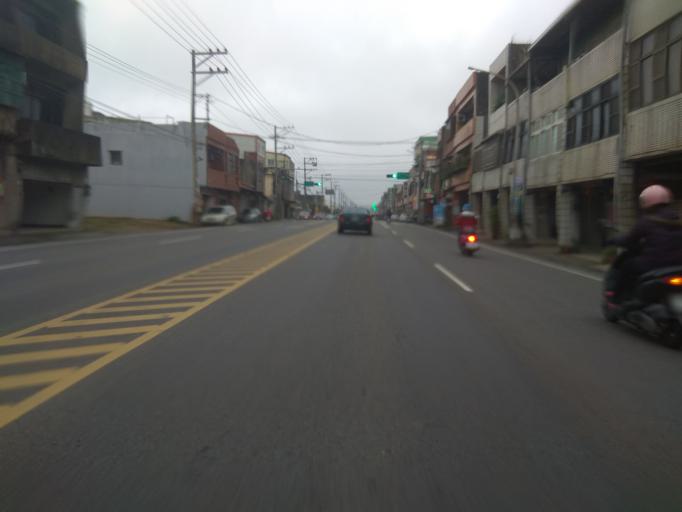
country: TW
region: Taiwan
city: Taoyuan City
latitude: 25.0251
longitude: 121.1131
